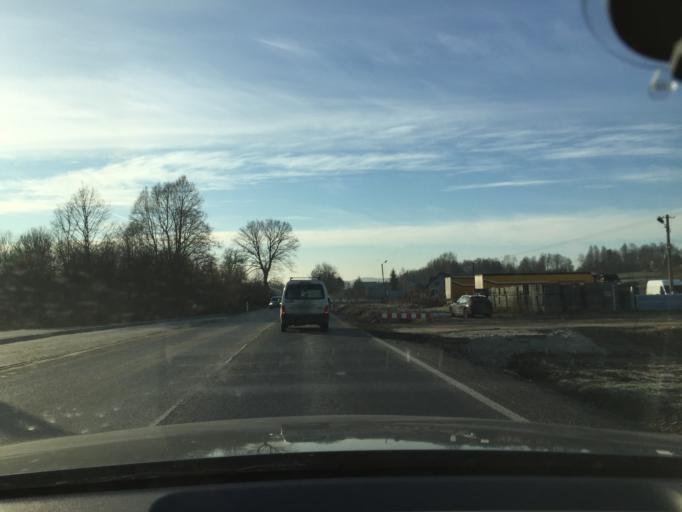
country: PL
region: Lesser Poland Voivodeship
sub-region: Powiat myslenicki
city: Glogoczow
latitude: 49.9043
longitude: 19.8547
